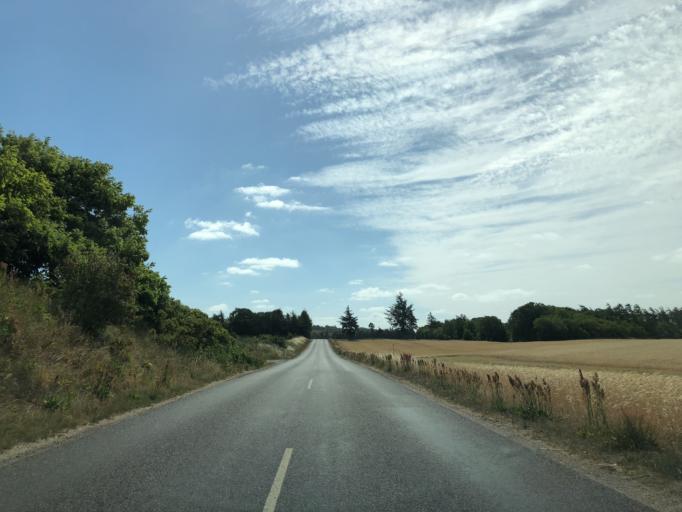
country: DK
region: North Denmark
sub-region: Vesthimmerland Kommune
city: Alestrup
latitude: 56.5783
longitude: 9.5108
